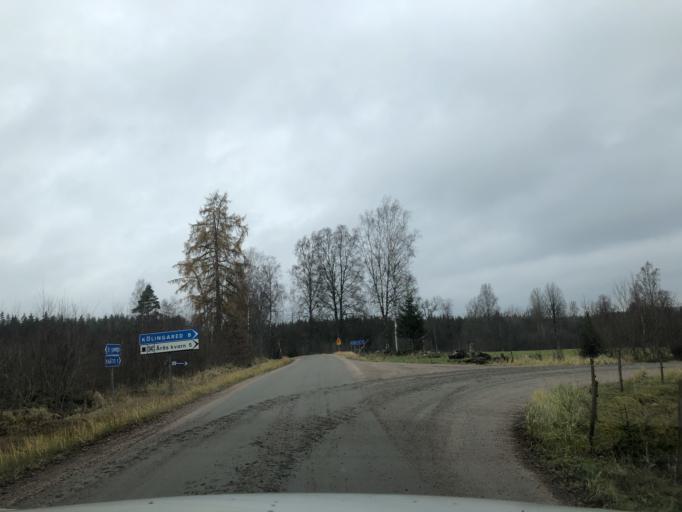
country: SE
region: Vaestra Goetaland
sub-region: Ulricehamns Kommun
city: Ulricehamn
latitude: 57.8523
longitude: 13.6333
